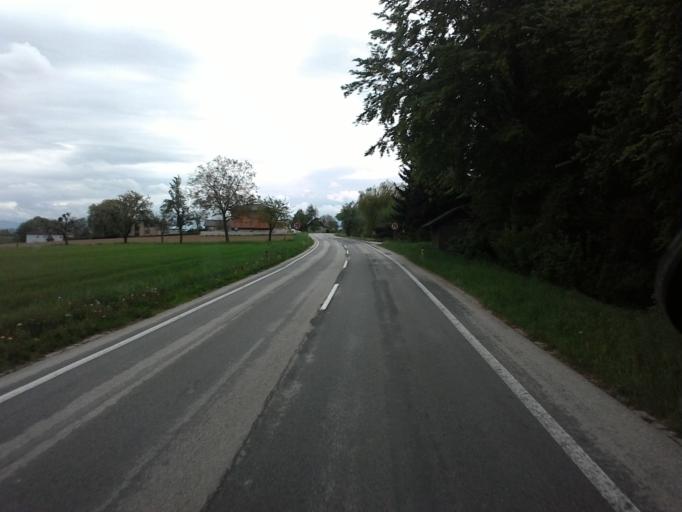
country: AT
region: Upper Austria
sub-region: Wels-Land
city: Sattledt
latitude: 48.0183
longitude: 14.0604
